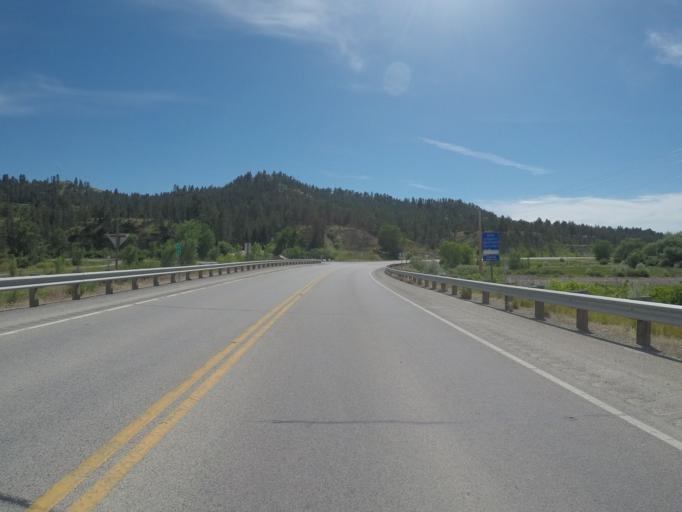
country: US
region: Montana
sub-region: Stillwater County
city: Columbus
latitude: 45.6275
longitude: -109.2566
